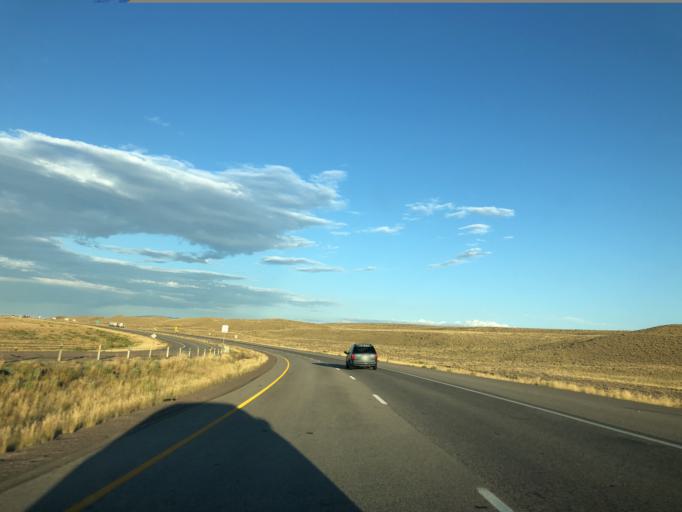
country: US
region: Wyoming
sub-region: Carbon County
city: Rawlins
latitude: 41.7752
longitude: -107.1192
